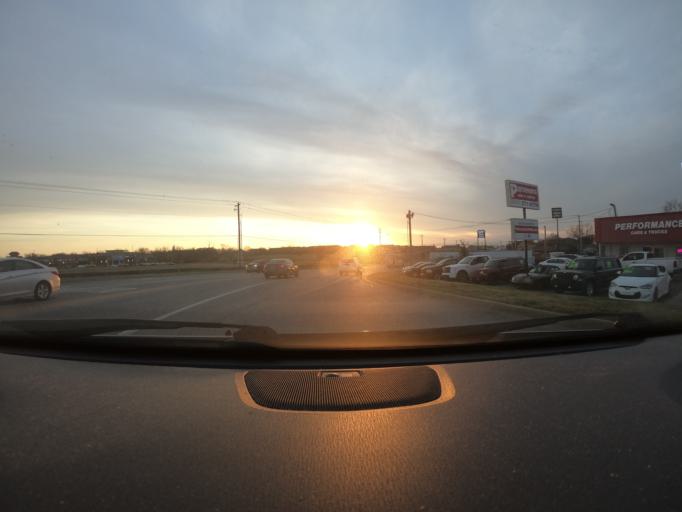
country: US
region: Arkansas
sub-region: Benton County
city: Bentonville
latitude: 36.3357
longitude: -94.2100
